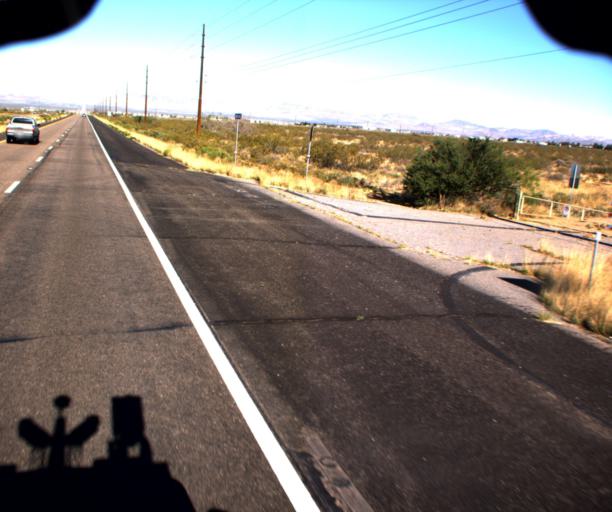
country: US
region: Arizona
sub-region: Mohave County
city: Golden Valley
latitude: 35.2225
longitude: -114.2240
